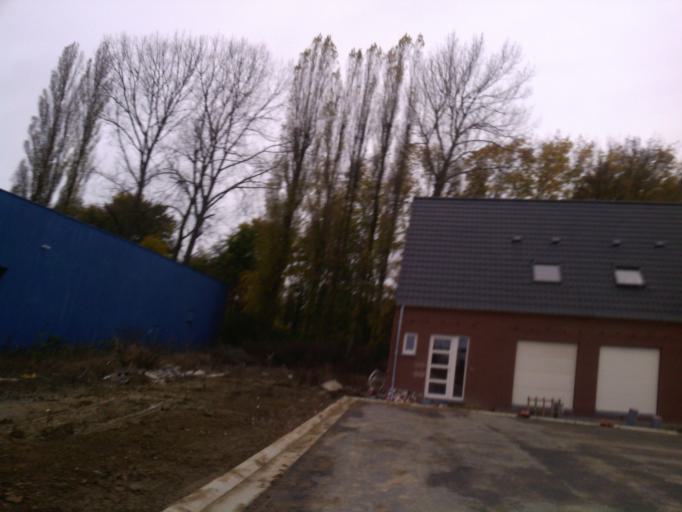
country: BE
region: Wallonia
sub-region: Province du Hainaut
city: Mouscron
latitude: 50.7593
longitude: 3.2242
